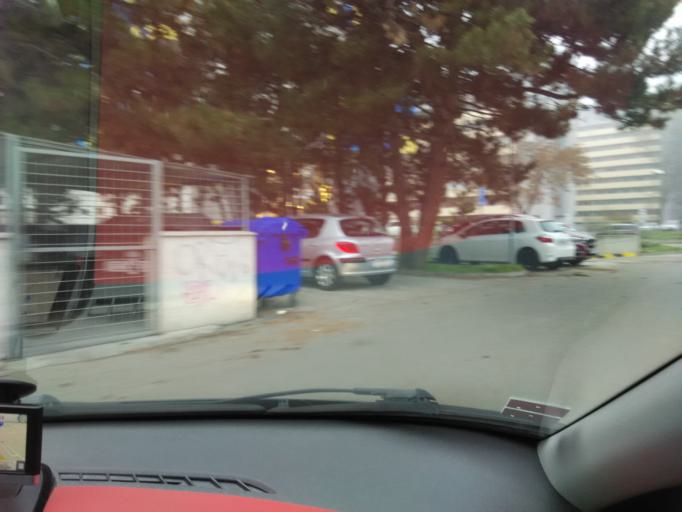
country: SK
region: Bratislavsky
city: Bratislava
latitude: 48.1537
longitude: 17.1628
